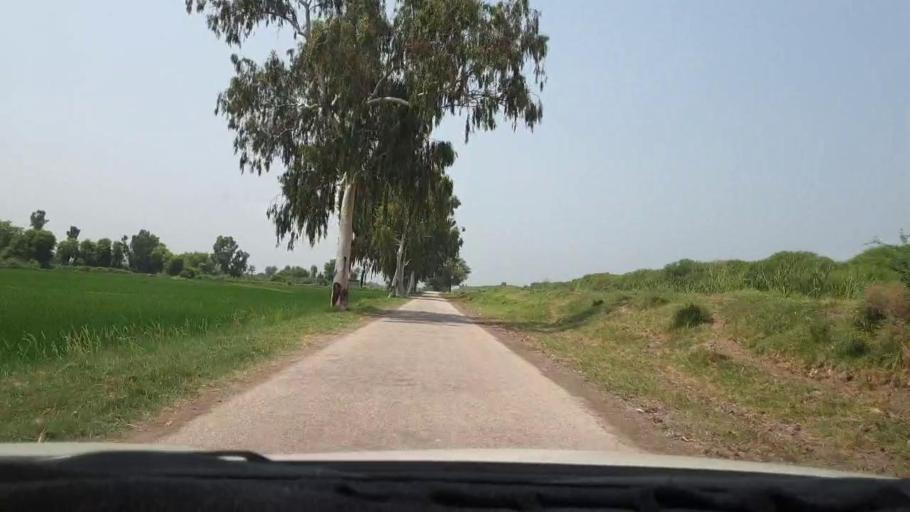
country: PK
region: Sindh
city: Dokri
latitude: 27.3138
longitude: 68.1025
